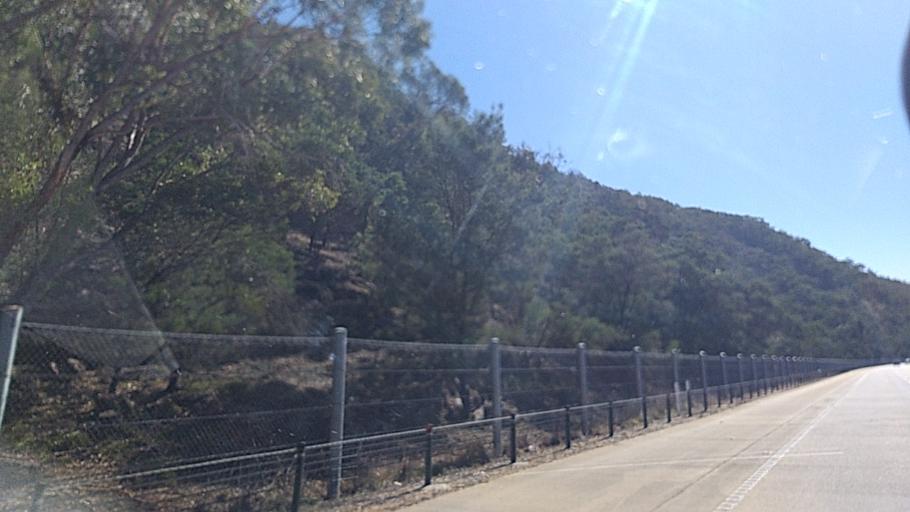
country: AU
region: New South Wales
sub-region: Yass Valley
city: Gundaroo
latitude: -35.0662
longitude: 149.3733
